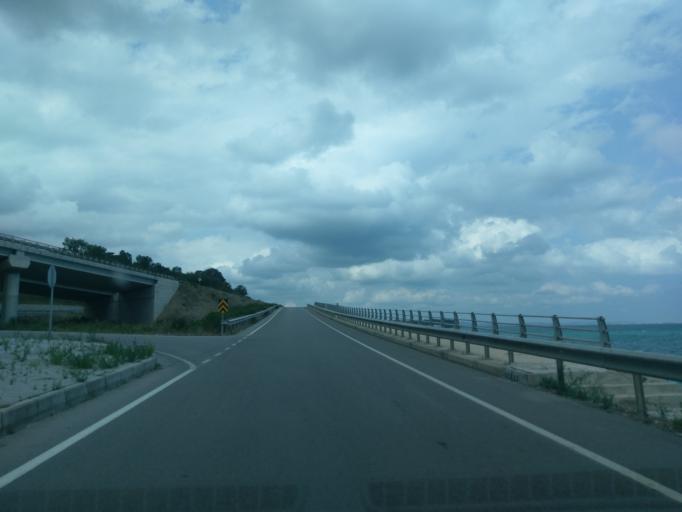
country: TR
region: Sinop
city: Gerze
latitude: 41.8243
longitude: 35.1679
